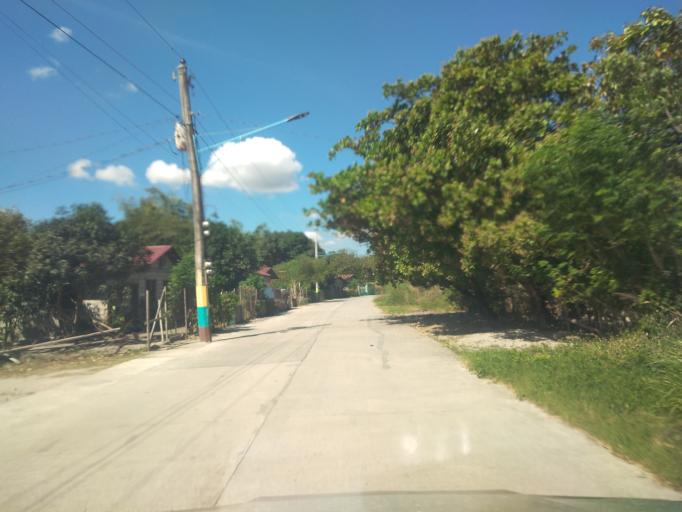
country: PH
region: Central Luzon
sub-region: Province of Pampanga
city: Santa Rita
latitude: 15.0311
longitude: 120.6257
